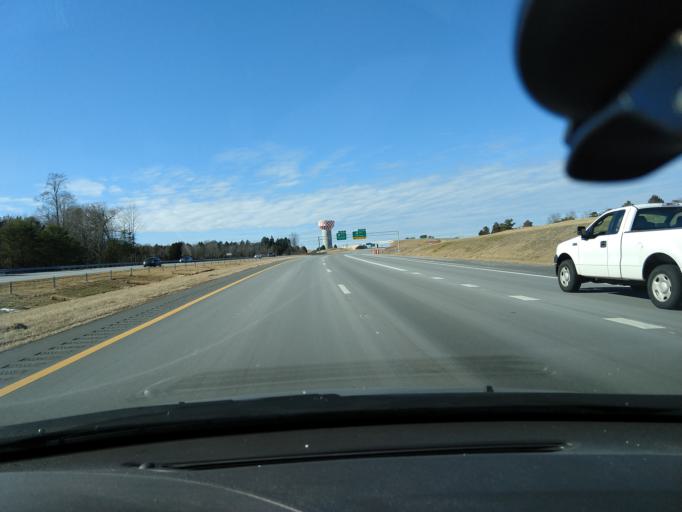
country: US
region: North Carolina
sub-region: Guilford County
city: Oak Ridge
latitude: 36.1205
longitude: -79.9514
